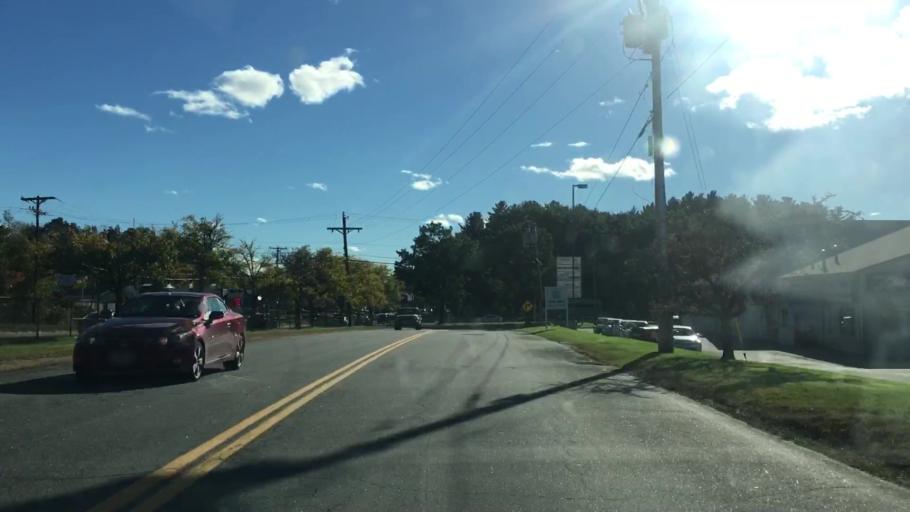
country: US
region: New Hampshire
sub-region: Merrimack County
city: South Hooksett
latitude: 43.0195
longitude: -71.4480
